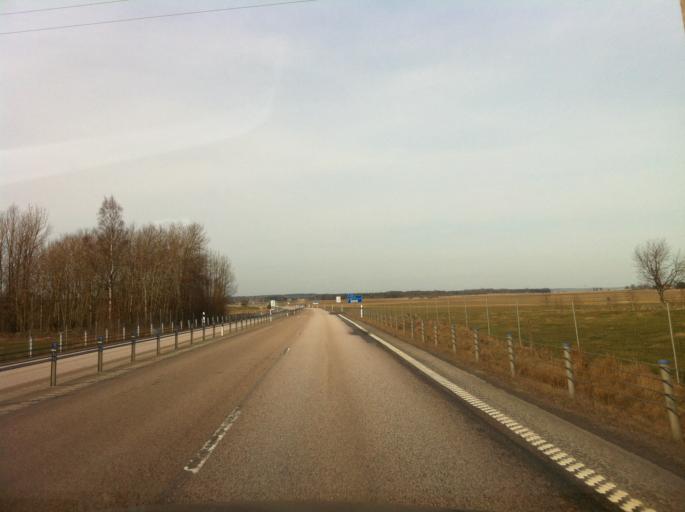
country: SE
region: Vaestra Goetaland
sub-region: Skovde Kommun
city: Stopen
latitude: 58.5467
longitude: 13.8108
